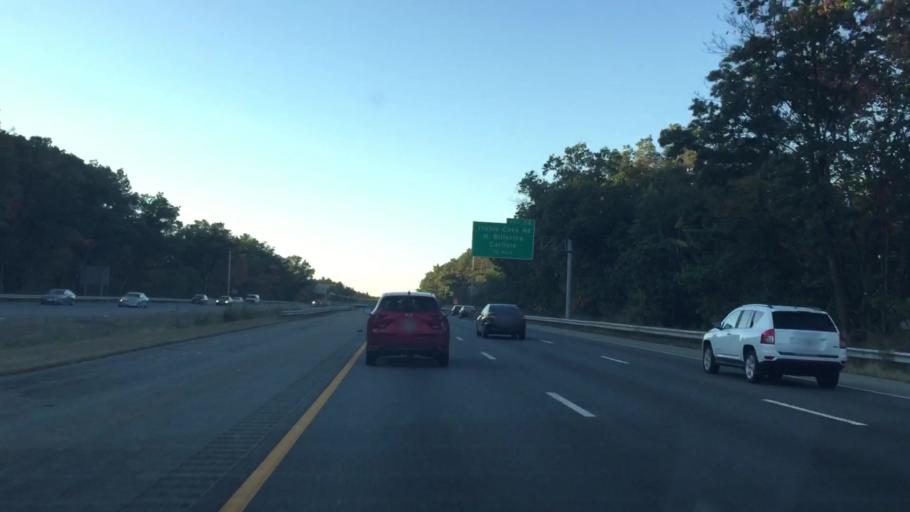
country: US
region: Massachusetts
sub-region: Middlesex County
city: Billerica
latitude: 42.5530
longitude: -71.2914
